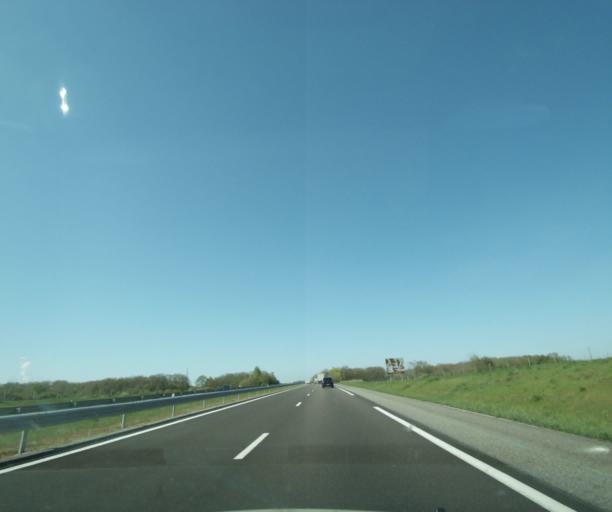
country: FR
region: Bourgogne
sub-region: Departement de la Nievre
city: Neuvy-sur-Loire
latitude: 47.4859
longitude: 2.9408
